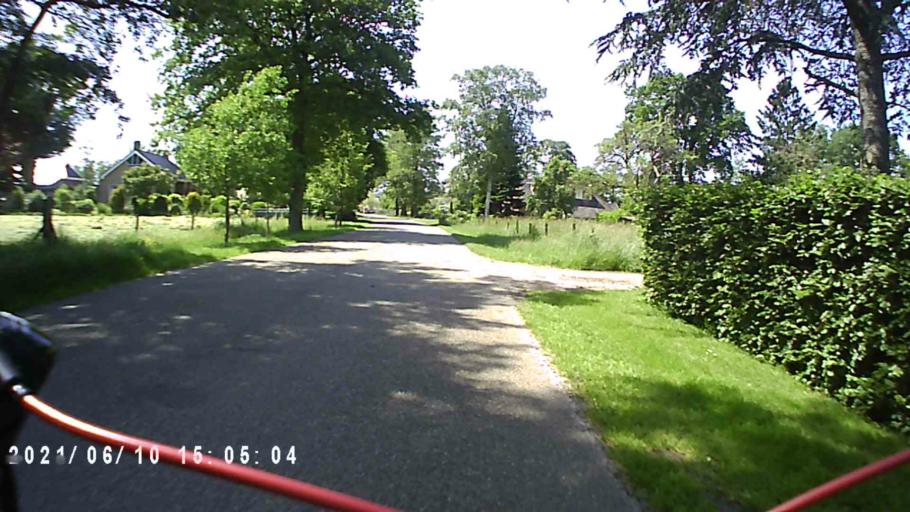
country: NL
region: Friesland
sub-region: Gemeente Achtkarspelen
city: Surhuizum
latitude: 53.1955
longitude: 6.2220
